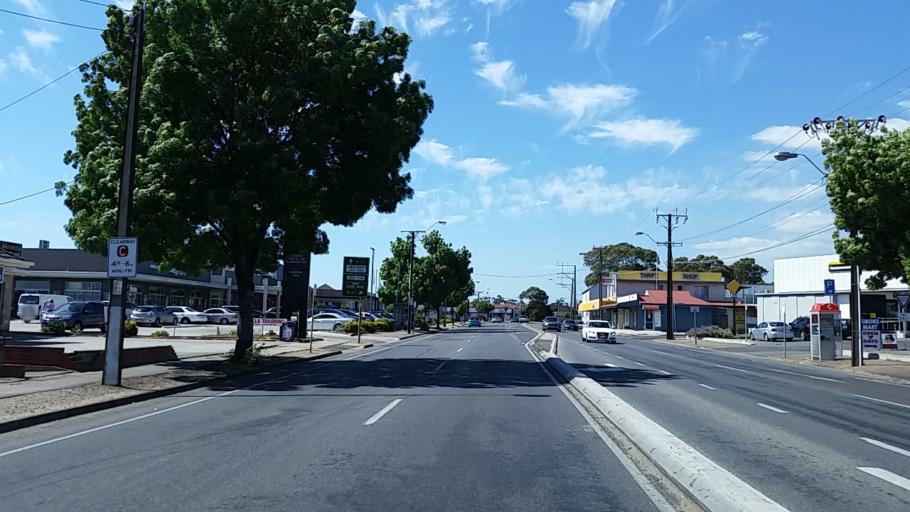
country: AU
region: South Australia
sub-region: Campbelltown
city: Campbelltown
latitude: -34.8782
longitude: 138.6636
